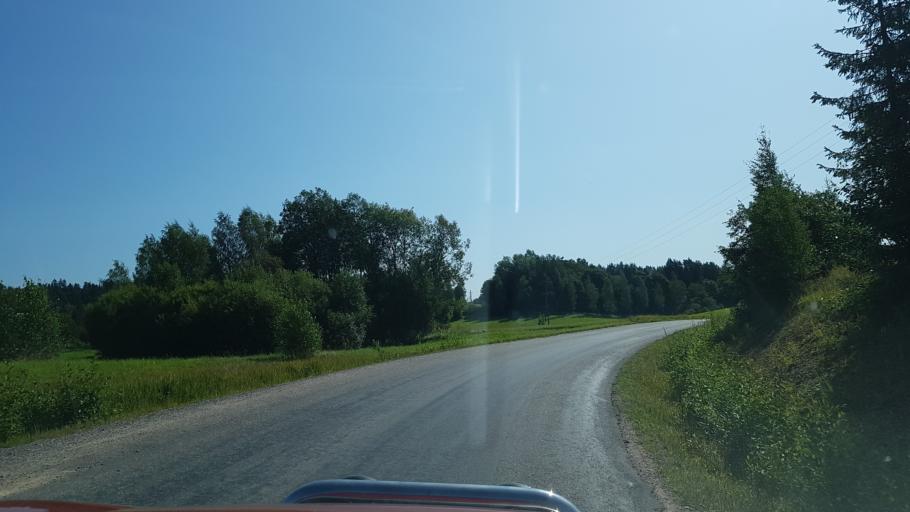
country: EE
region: Vorumaa
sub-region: Voru linn
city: Voru
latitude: 57.7196
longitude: 27.0786
